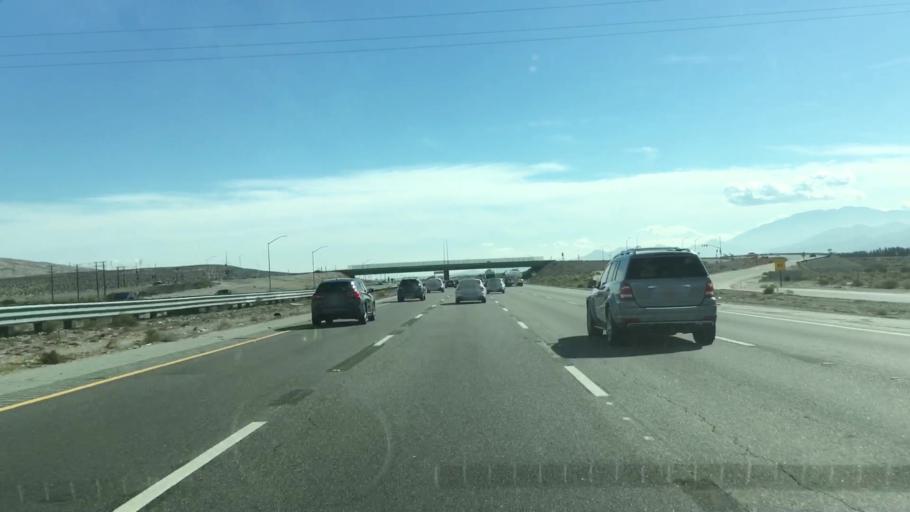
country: US
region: California
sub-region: Riverside County
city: Garnet
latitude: 33.8822
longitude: -116.5071
